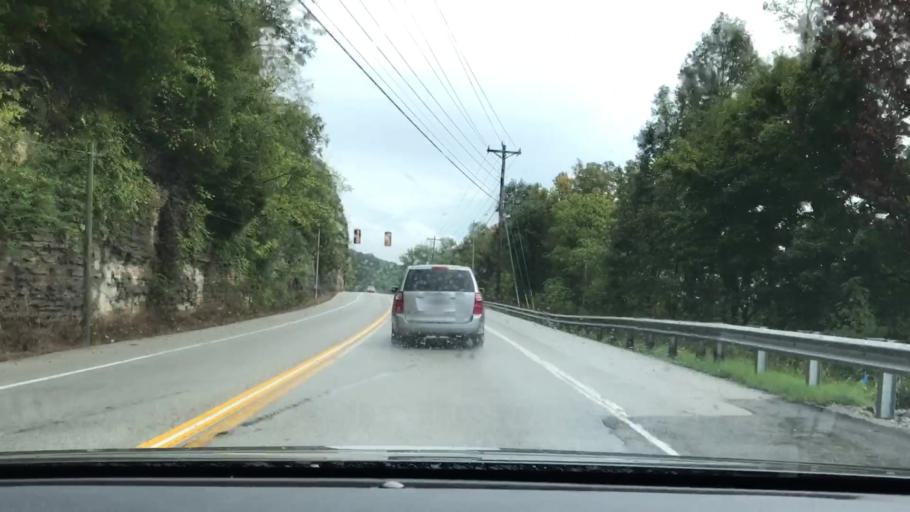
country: US
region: Tennessee
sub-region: Smith County
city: Carthage
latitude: 36.2687
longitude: -85.9662
